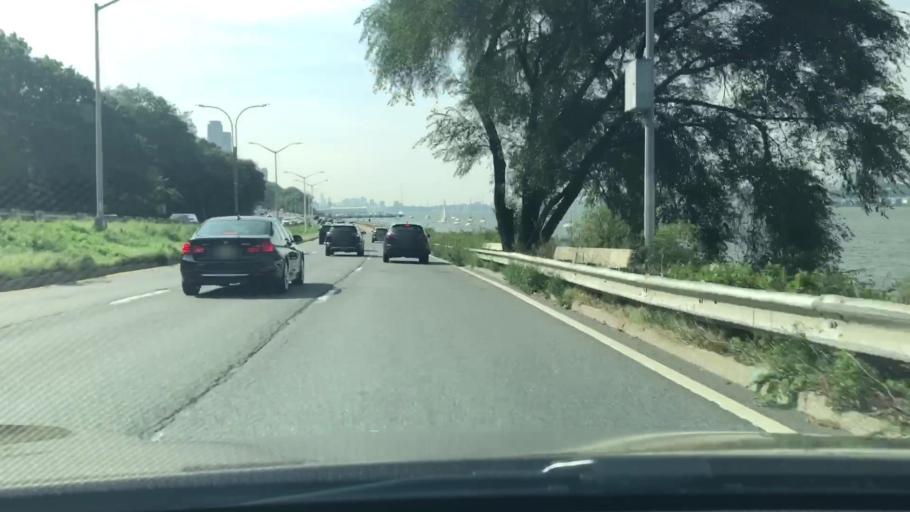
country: US
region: New York
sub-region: New York County
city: Manhattan
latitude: 40.7935
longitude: -73.9795
